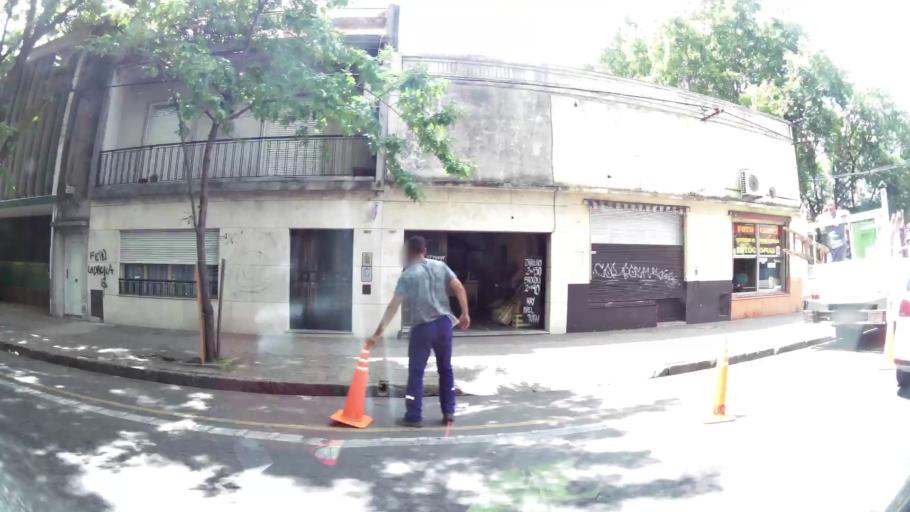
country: AR
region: Santa Fe
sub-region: Departamento de Rosario
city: Rosario
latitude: -32.9750
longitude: -60.6350
